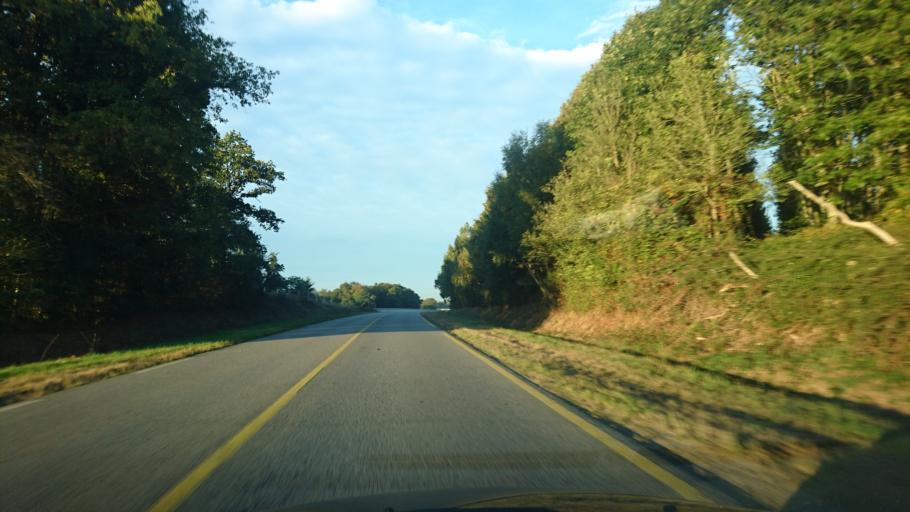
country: FR
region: Brittany
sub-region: Departement d'Ille-et-Vilaine
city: Sainte-Marie
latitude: 47.7124
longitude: -1.9856
